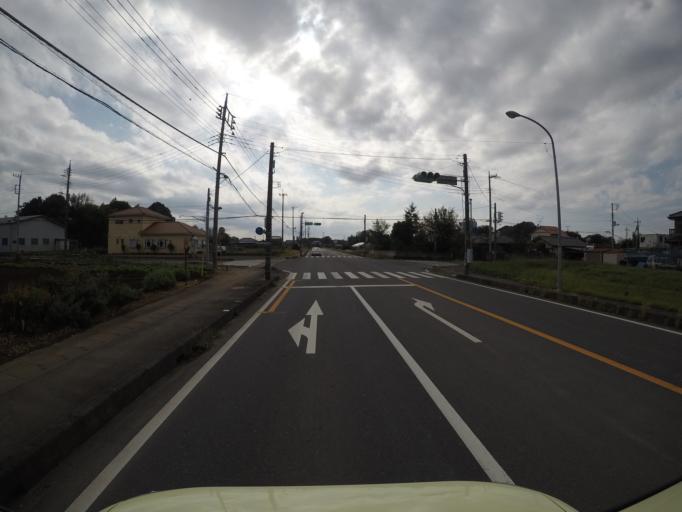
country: JP
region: Ibaraki
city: Mitsukaido
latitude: 35.9954
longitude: 139.9325
